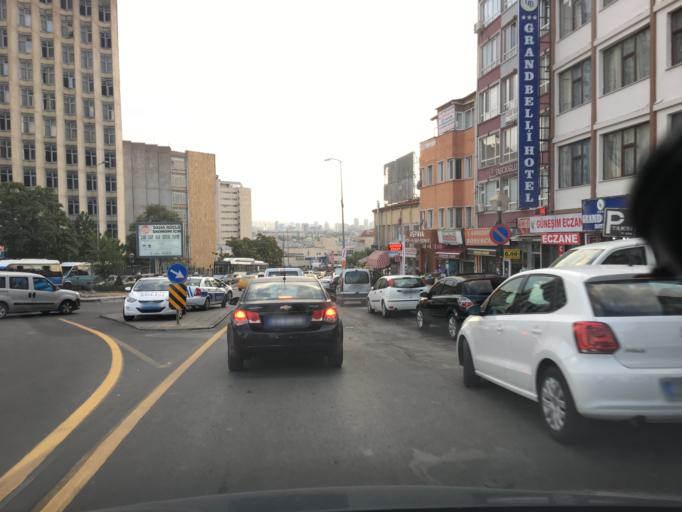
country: TR
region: Ankara
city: Ankara
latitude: 39.9340
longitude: 32.8612
